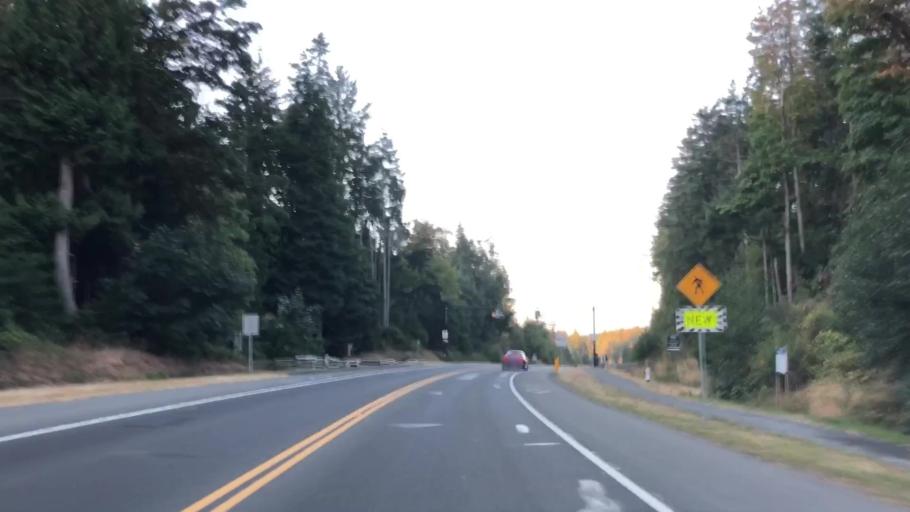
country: CA
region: British Columbia
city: Colwood
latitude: 48.4147
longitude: -123.5047
